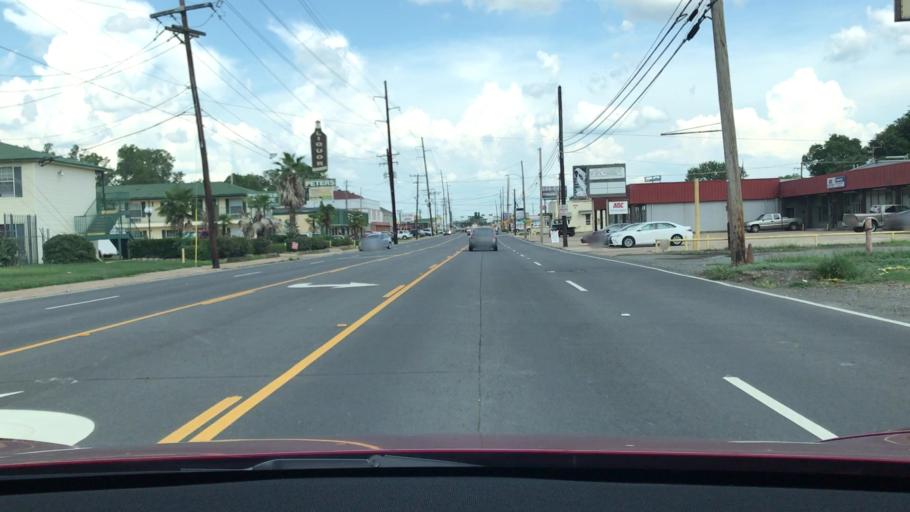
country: US
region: Louisiana
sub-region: Bossier Parish
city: Bossier City
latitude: 32.5158
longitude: -93.7239
